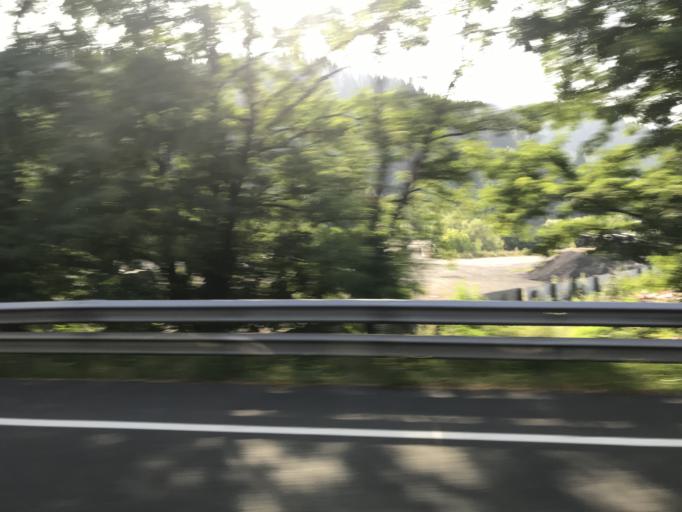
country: ES
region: Basque Country
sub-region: Provincia de Guipuzcoa
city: Villafranca de Ordizia
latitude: 43.0572
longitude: -2.1709
